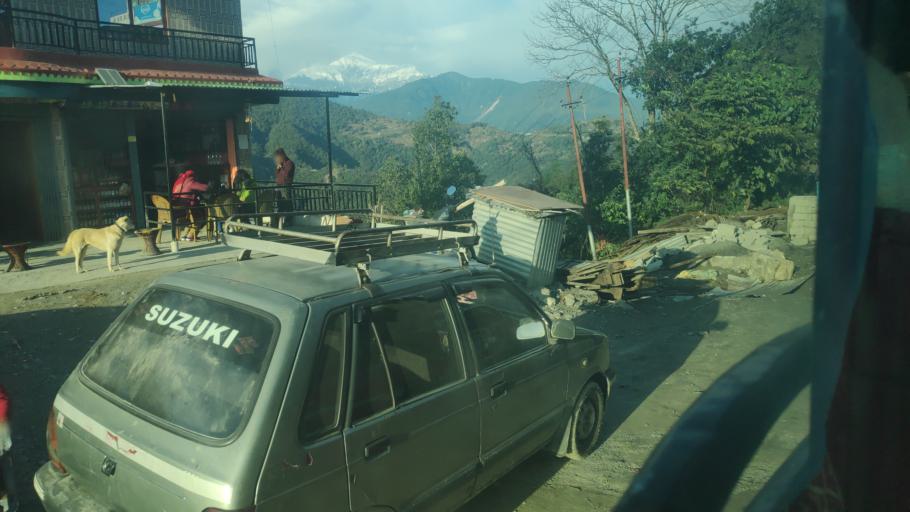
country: NP
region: Western Region
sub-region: Gandaki Zone
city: Pokhara
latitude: 28.2817
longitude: 83.8671
